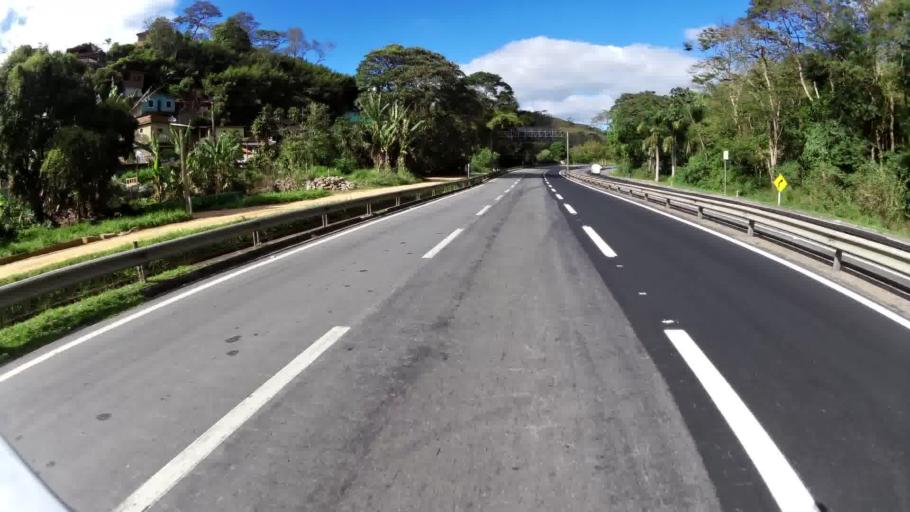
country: BR
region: Rio de Janeiro
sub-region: Areal
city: Areal
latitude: -22.2854
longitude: -43.1209
